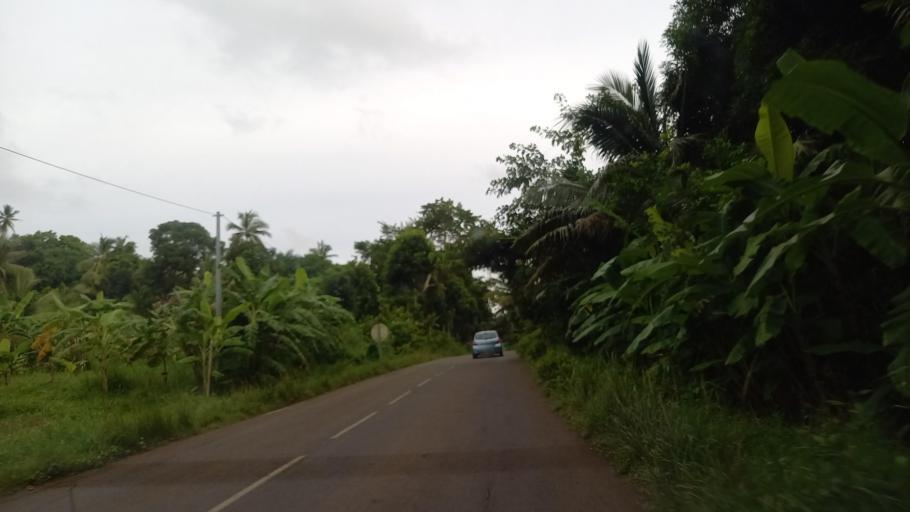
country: YT
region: Sada
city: Sada
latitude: -12.8742
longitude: 45.1208
